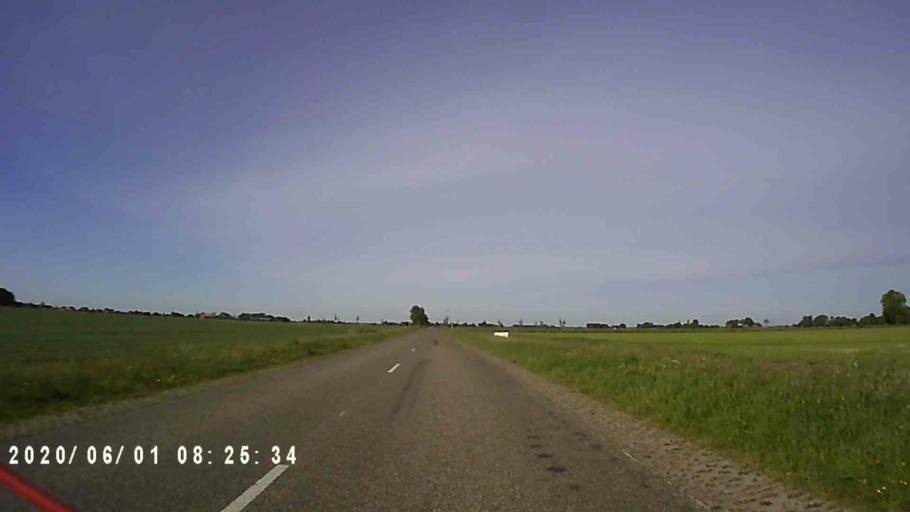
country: NL
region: Friesland
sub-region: Gemeente Ferwerderadiel
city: Burdaard
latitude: 53.3002
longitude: 5.8647
